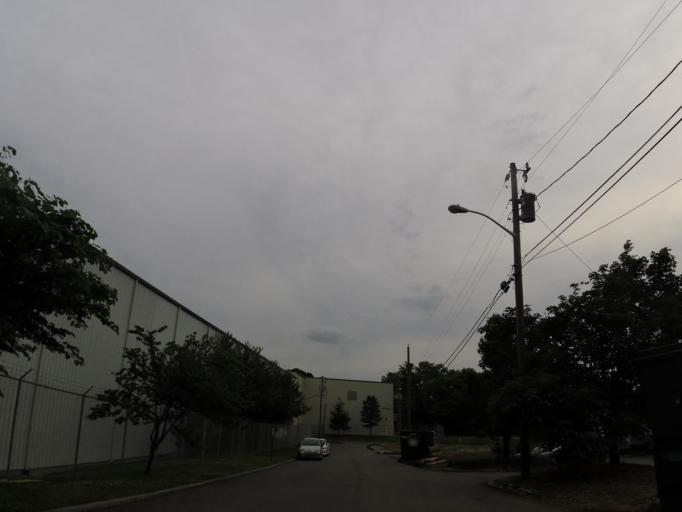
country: US
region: Tennessee
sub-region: Knox County
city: Knoxville
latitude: 35.9526
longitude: -83.9628
